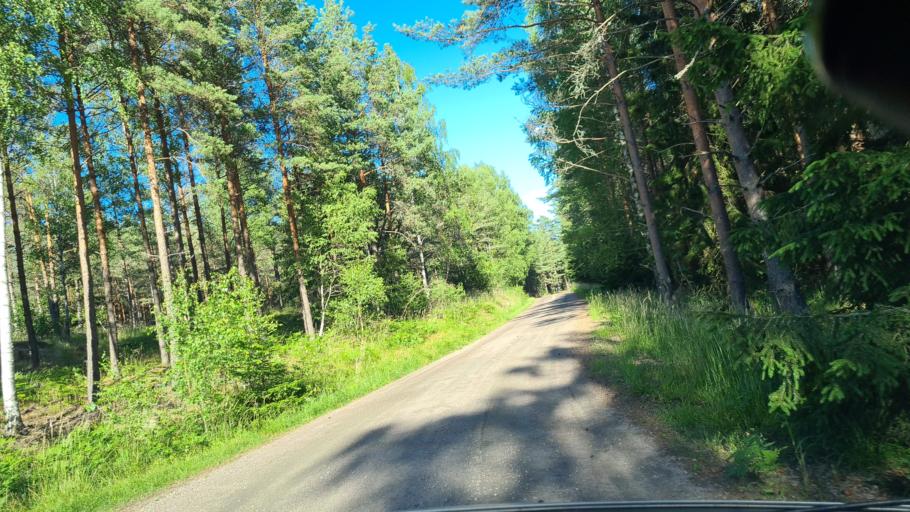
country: SE
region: Soedermanland
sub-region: Nykopings Kommun
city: Nykoping
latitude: 58.9113
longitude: 16.9435
